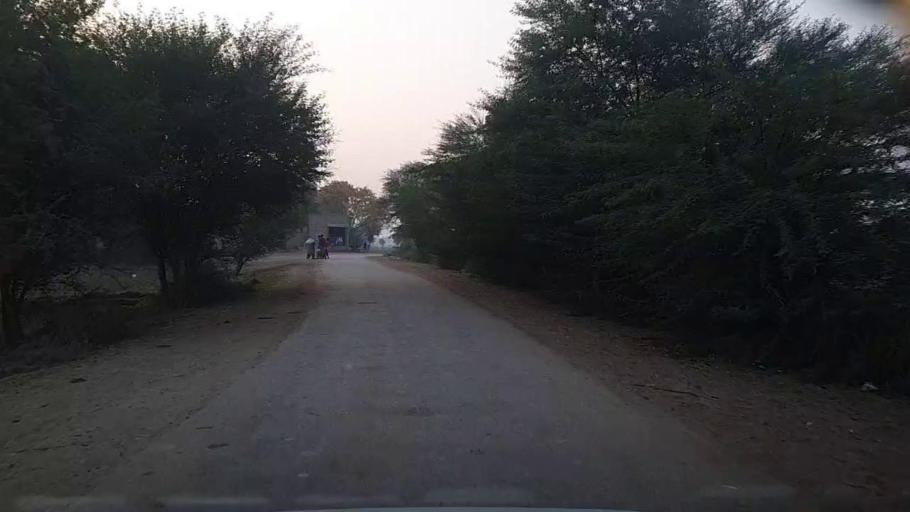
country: PK
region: Sindh
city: Bozdar
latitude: 27.0566
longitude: 68.5971
